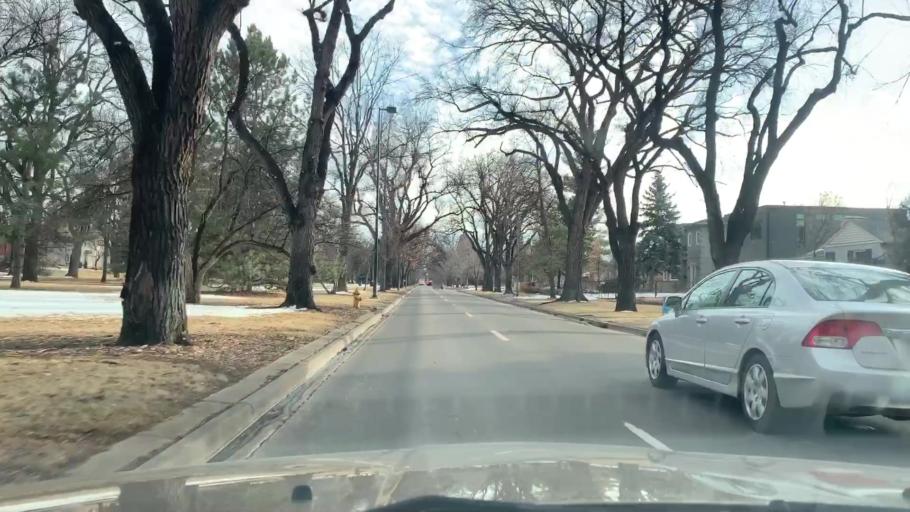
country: US
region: Colorado
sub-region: Arapahoe County
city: Glendale
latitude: 39.7329
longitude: -104.9128
